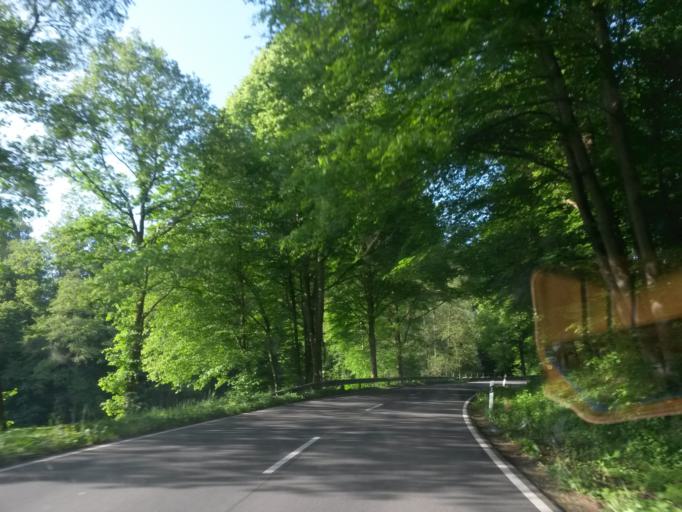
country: DE
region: North Rhine-Westphalia
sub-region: Regierungsbezirk Koln
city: Much
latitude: 50.8787
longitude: 7.3513
